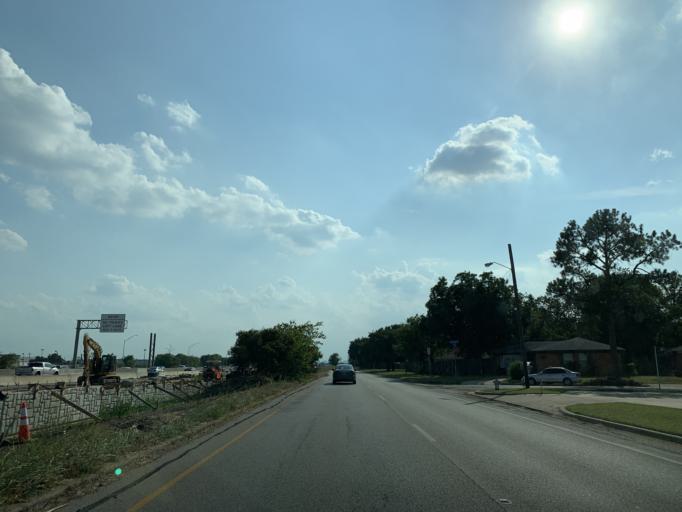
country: US
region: Texas
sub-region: Tarrant County
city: Richland Hills
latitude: 32.8005
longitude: -97.2239
